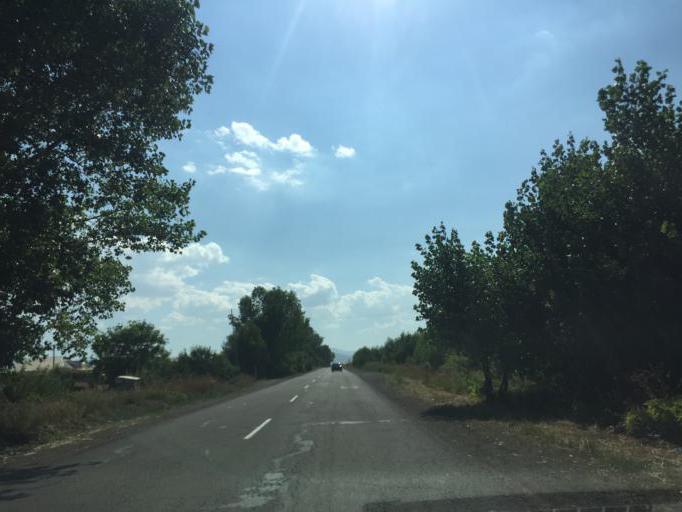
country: AM
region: Geghark'unik'i Marz
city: Tsovinar
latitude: 40.1595
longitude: 45.4540
